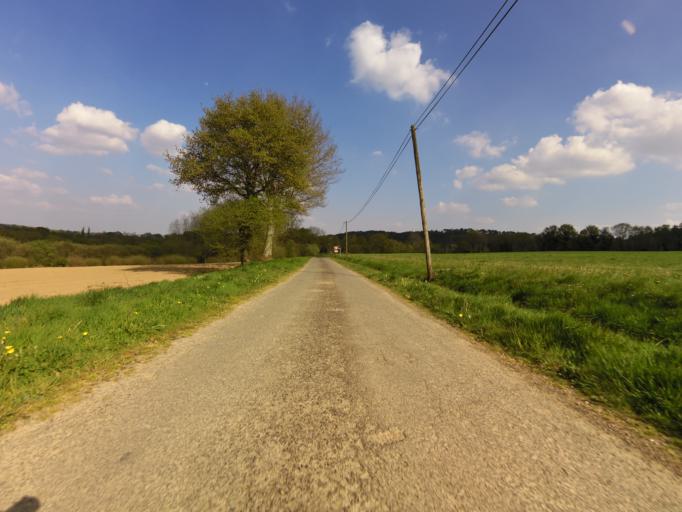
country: FR
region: Brittany
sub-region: Departement du Morbihan
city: Pluherlin
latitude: 47.7098
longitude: -2.3405
